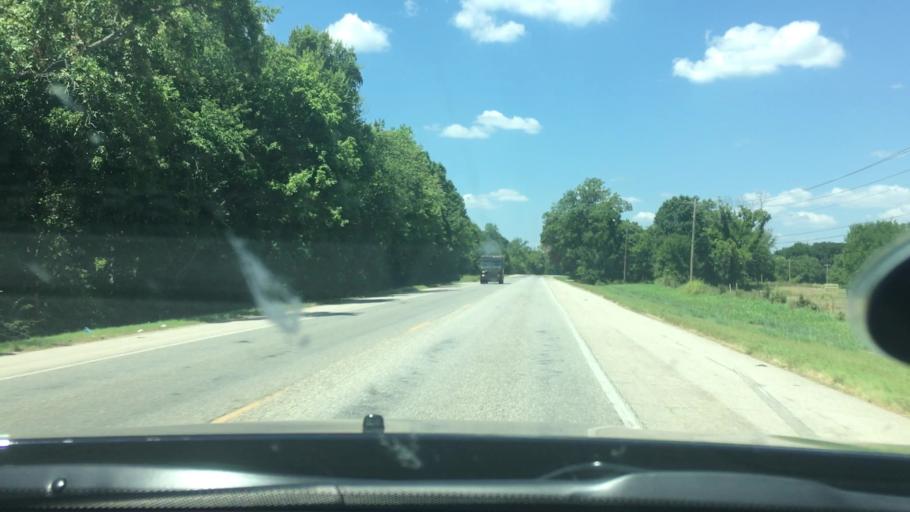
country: US
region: Oklahoma
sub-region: Marshall County
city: Oakland
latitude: 34.1735
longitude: -96.8477
